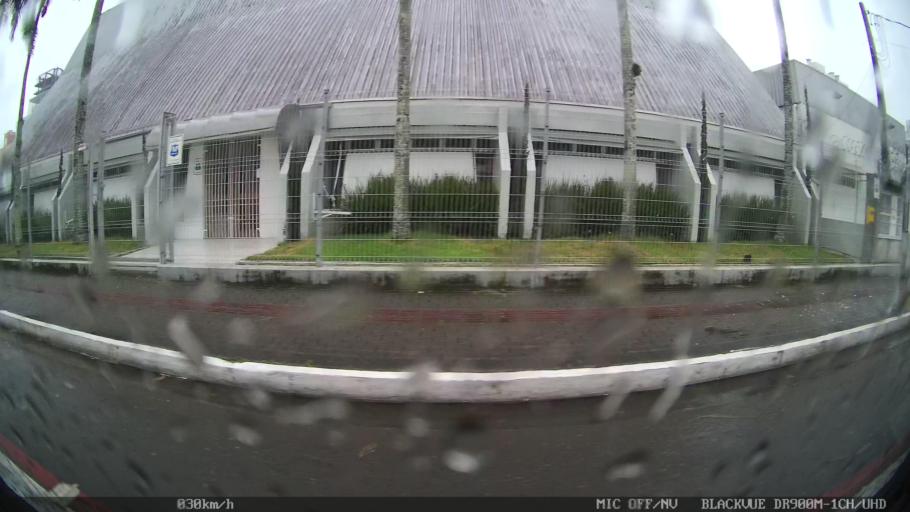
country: BR
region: Santa Catarina
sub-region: Itajai
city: Itajai
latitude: -26.9083
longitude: -48.6701
